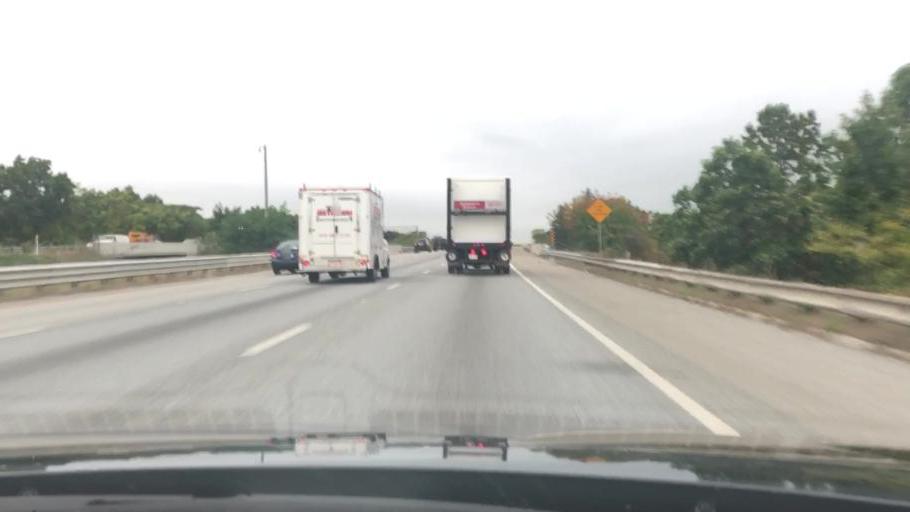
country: US
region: Massachusetts
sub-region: Middlesex County
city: Lowell
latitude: 42.6190
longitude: -71.2882
